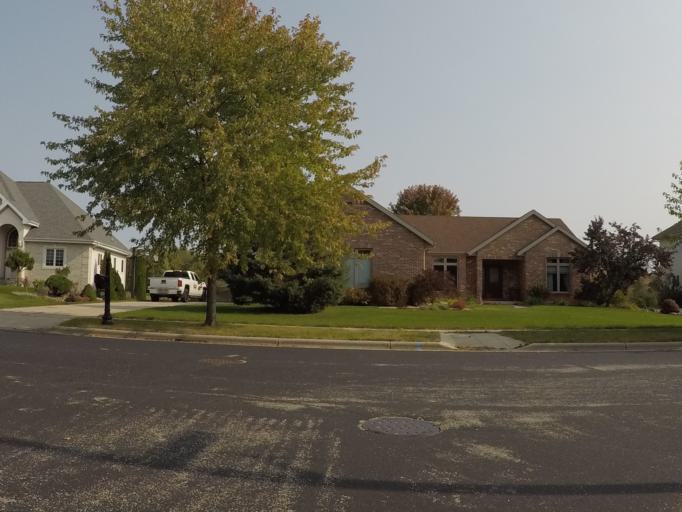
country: US
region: Wisconsin
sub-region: Dane County
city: Verona
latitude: 43.0365
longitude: -89.5357
